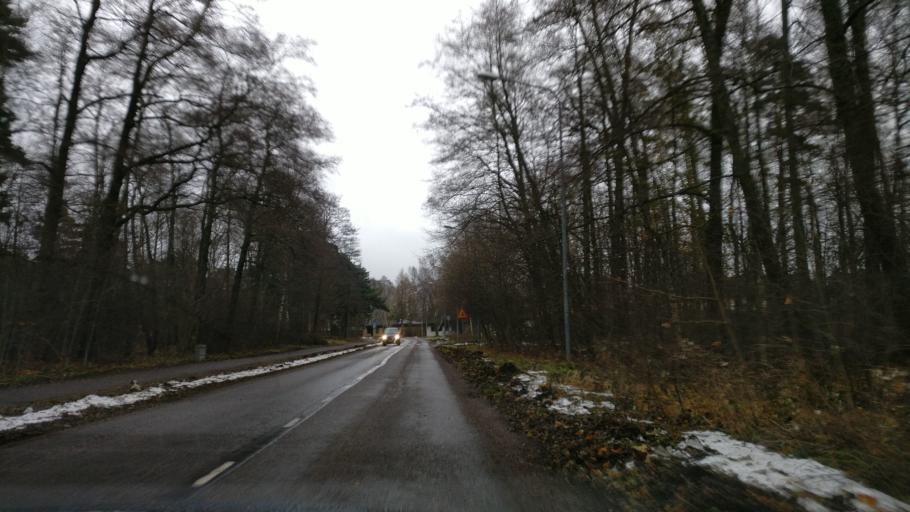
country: FI
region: Uusimaa
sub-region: Raaseporin
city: Hanko
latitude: 59.8332
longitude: 22.9351
